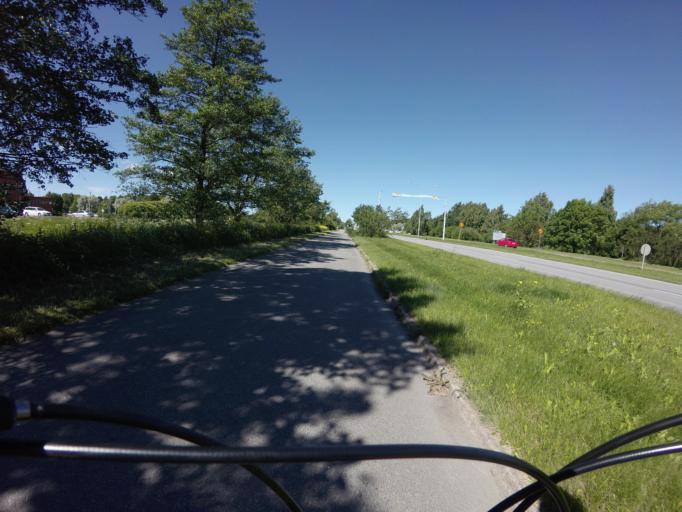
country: FI
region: Varsinais-Suomi
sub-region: Turku
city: Turku
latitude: 60.4567
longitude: 22.2326
